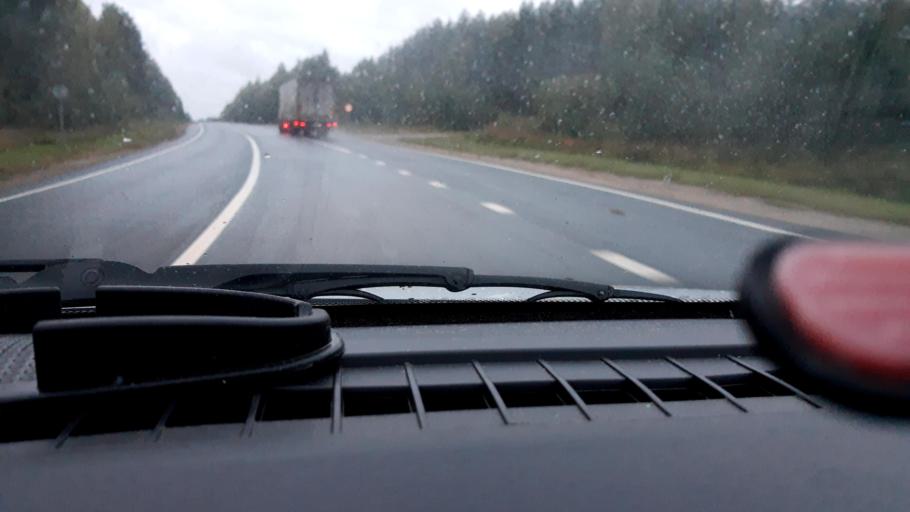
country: RU
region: Nizjnij Novgorod
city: Krasnyye Baki
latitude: 57.0285
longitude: 45.1153
